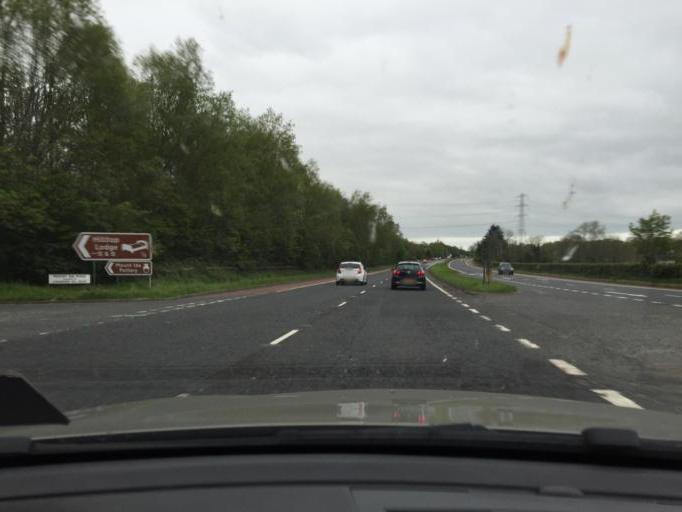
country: GB
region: Northern Ireland
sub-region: Banbridge District
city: Banbridge
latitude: 54.3799
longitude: -6.1899
